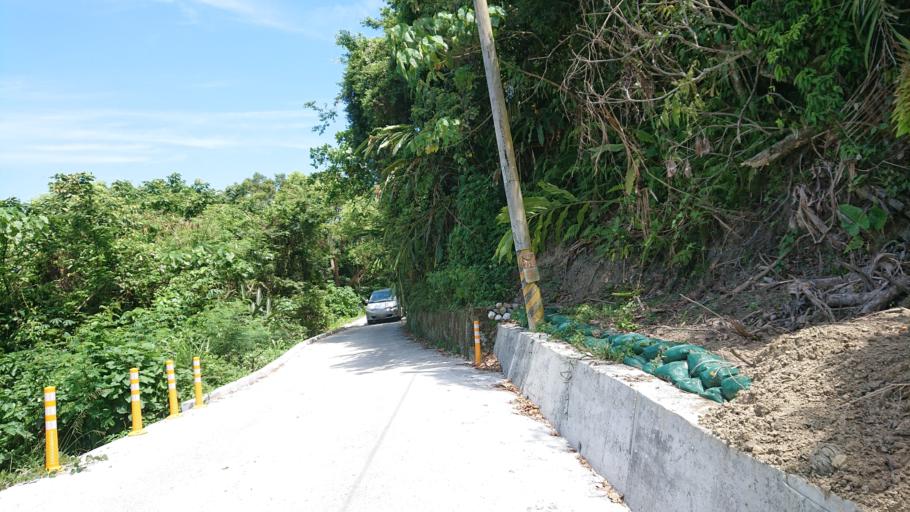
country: TW
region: Taiwan
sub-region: Hualien
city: Hualian
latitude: 23.7679
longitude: 121.5614
